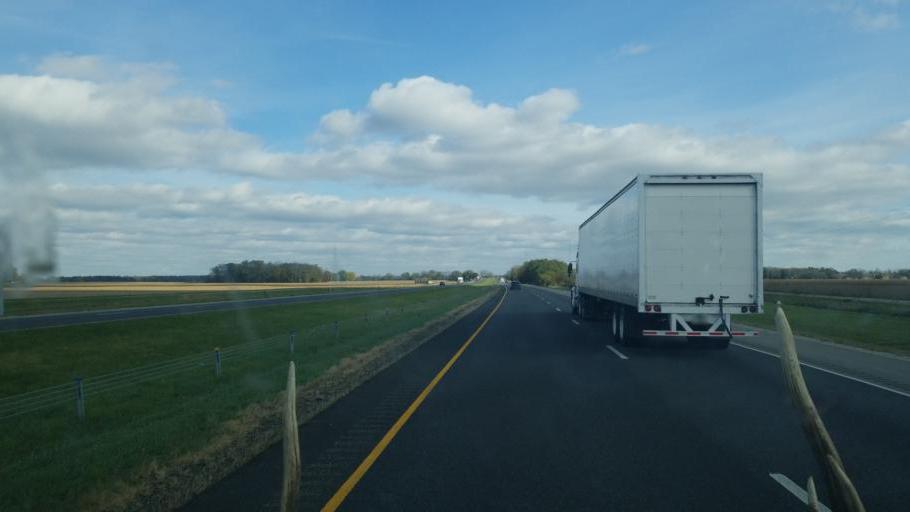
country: US
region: Indiana
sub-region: Wayne County
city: Cambridge City
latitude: 39.8527
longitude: -85.1195
